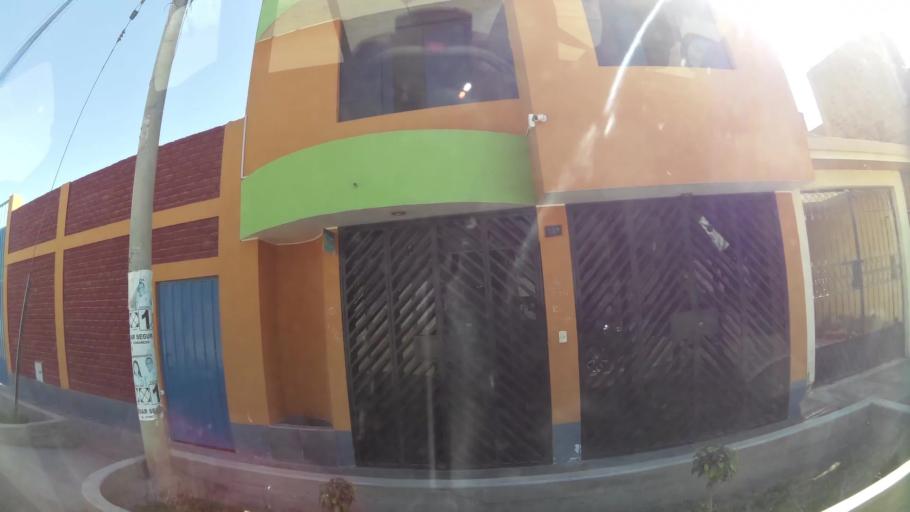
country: PE
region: Ica
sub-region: Provincia de Ica
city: La Tinguina
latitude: -14.0384
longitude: -75.7055
